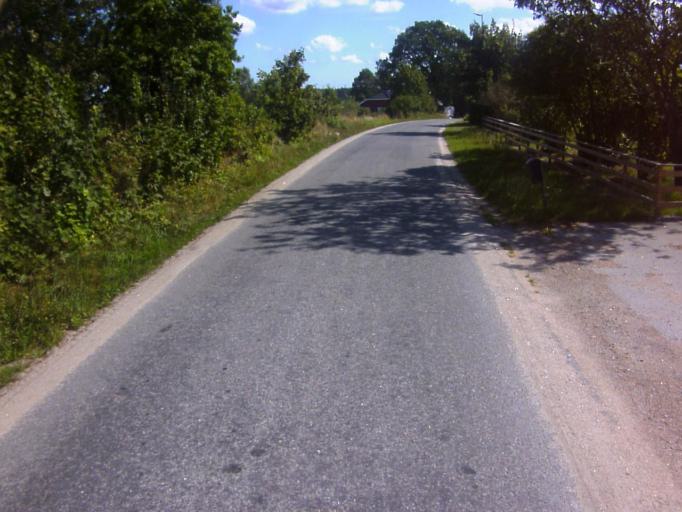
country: SE
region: Blekinge
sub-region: Olofstroms Kommun
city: Jamshog
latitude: 56.1986
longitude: 14.6072
